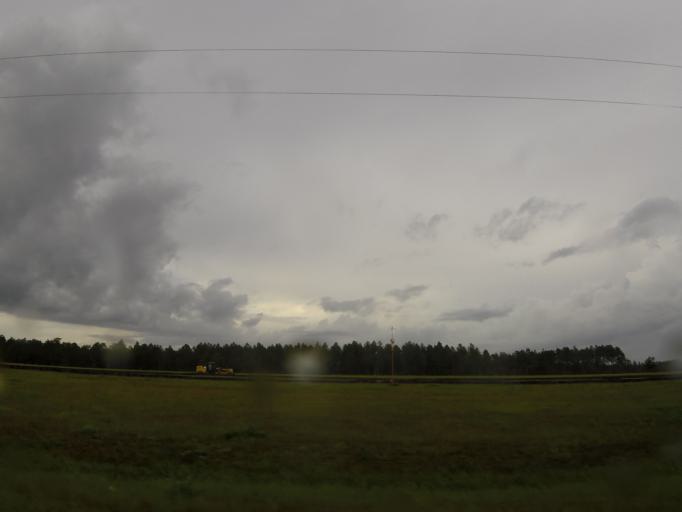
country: US
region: Georgia
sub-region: Wayne County
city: Jesup
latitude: 31.5524
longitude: -81.8830
